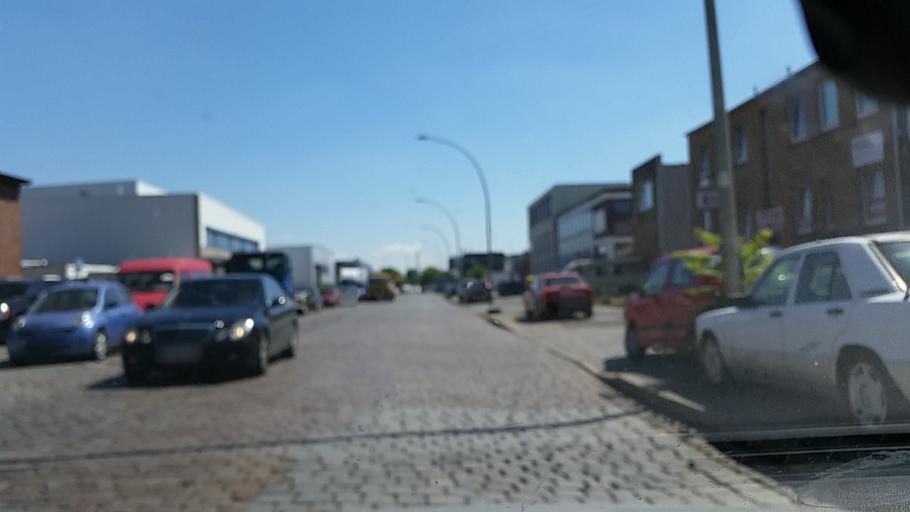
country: DE
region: Hamburg
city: Rothenburgsort
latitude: 53.5380
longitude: 10.0508
